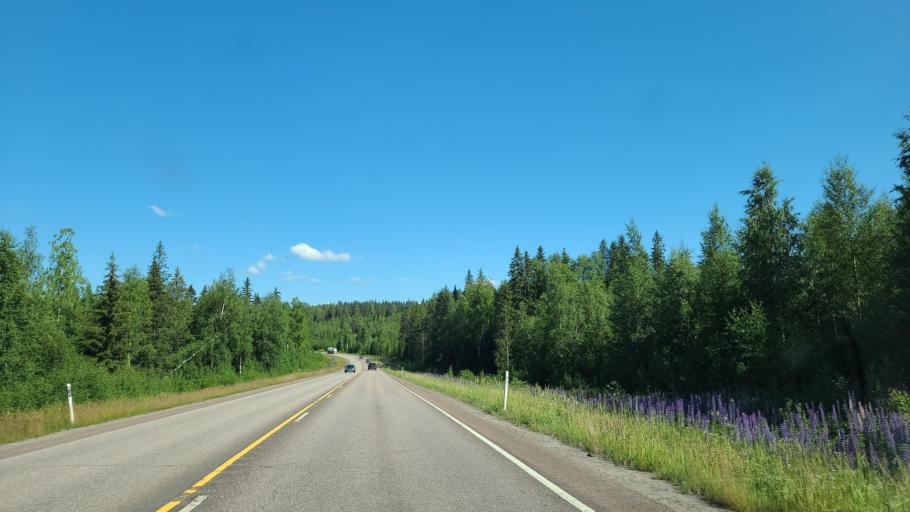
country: FI
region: Central Finland
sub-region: Jyvaeskylae
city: Petaejaevesi
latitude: 62.2727
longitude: 25.3672
